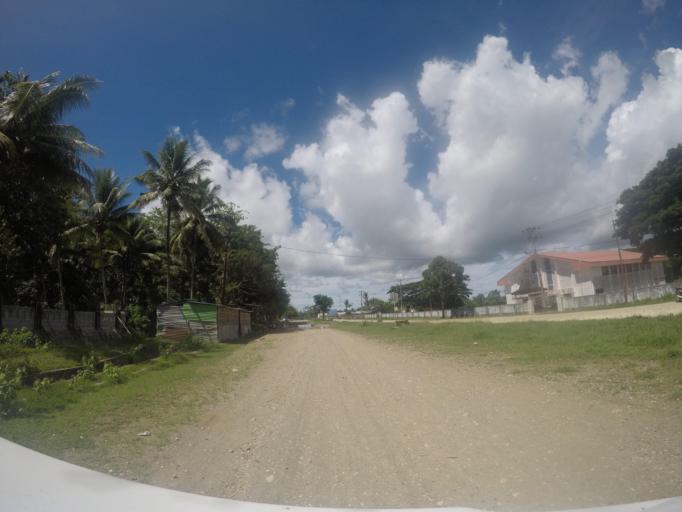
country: TL
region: Lautem
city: Lospalos
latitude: -8.4933
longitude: 126.9924
